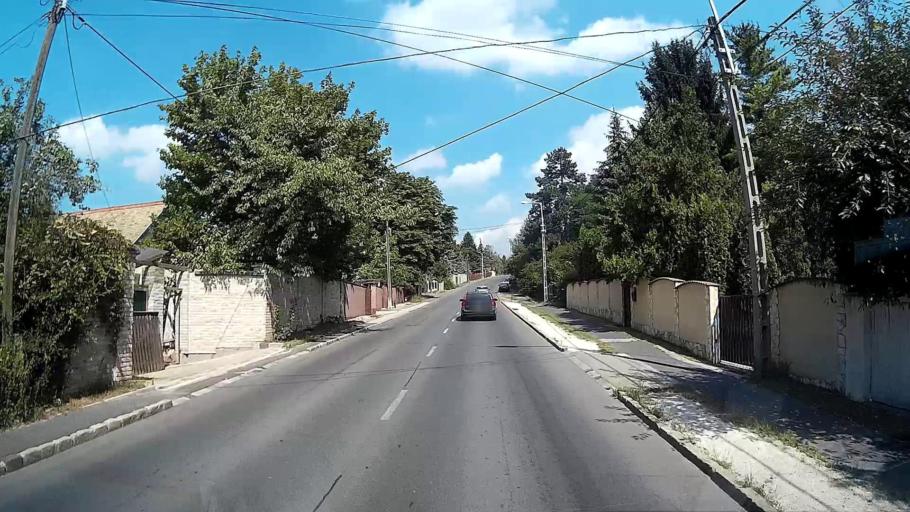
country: HU
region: Pest
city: Solymar
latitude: 47.5539
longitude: 18.9490
